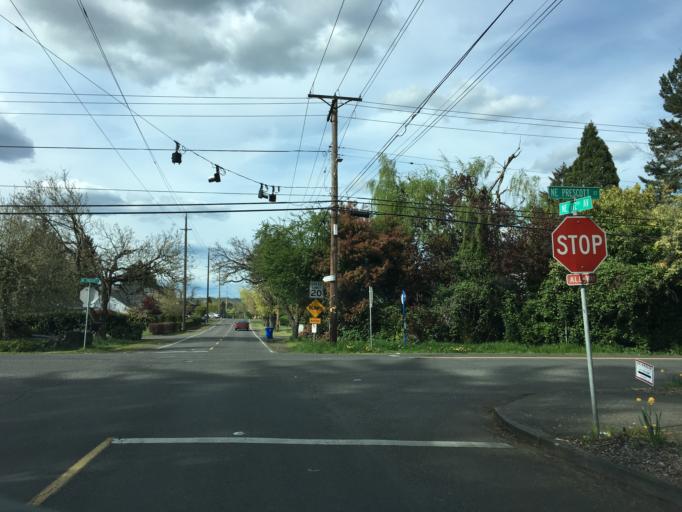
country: US
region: Oregon
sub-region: Multnomah County
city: Lents
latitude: 45.5552
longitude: -122.5474
